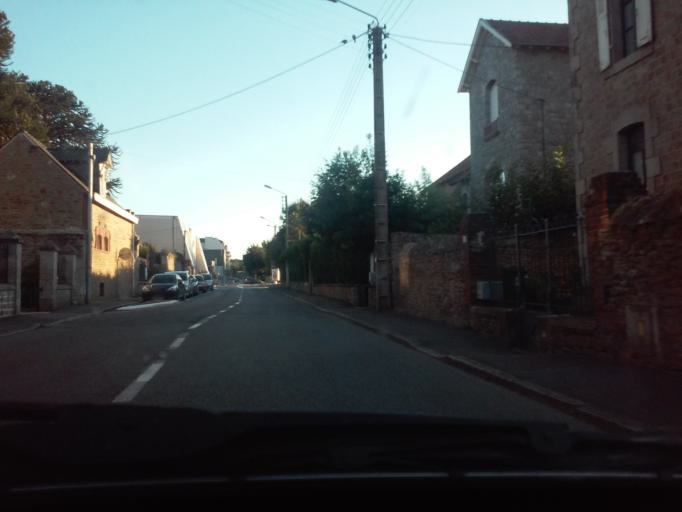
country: FR
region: Brittany
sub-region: Departement des Cotes-d'Armor
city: Lehon
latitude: 48.4614
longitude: -2.0471
